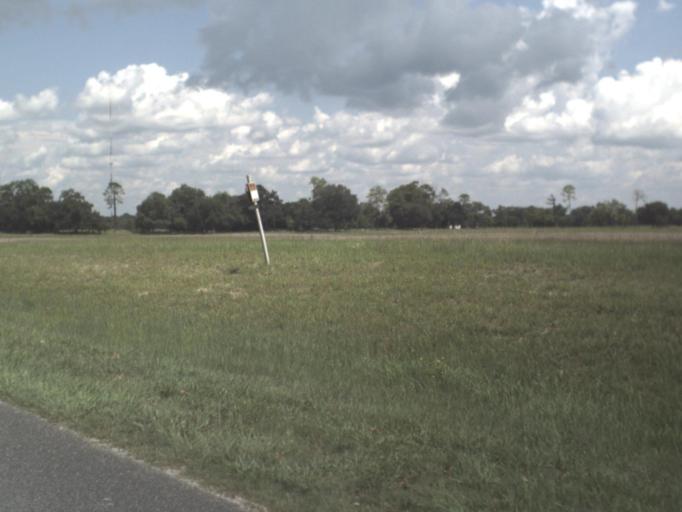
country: US
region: Florida
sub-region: Gilchrist County
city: Trenton
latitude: 29.6129
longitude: -82.8604
